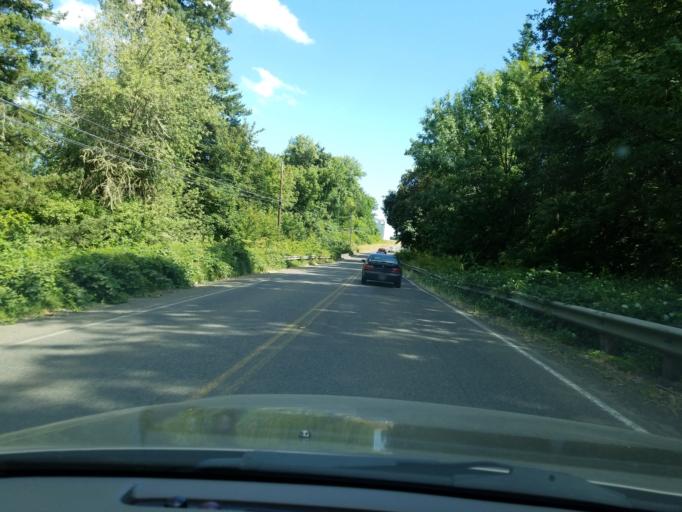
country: US
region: Oregon
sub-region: Yamhill County
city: McMinnville
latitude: 45.2541
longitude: -123.2022
